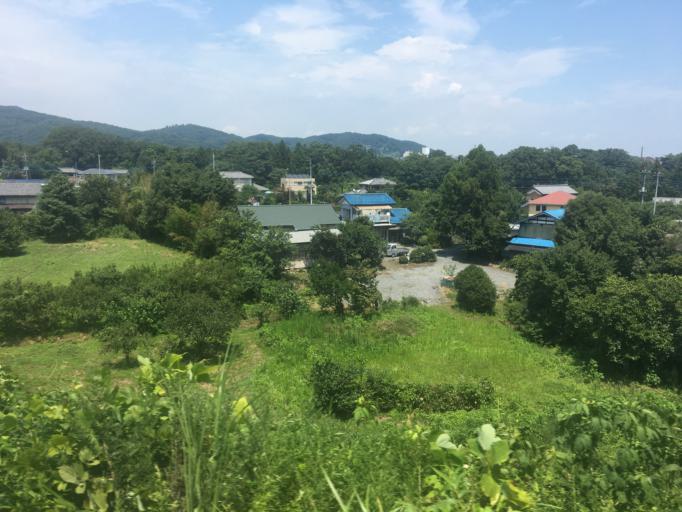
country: JP
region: Saitama
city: Yorii
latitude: 36.1081
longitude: 139.1876
